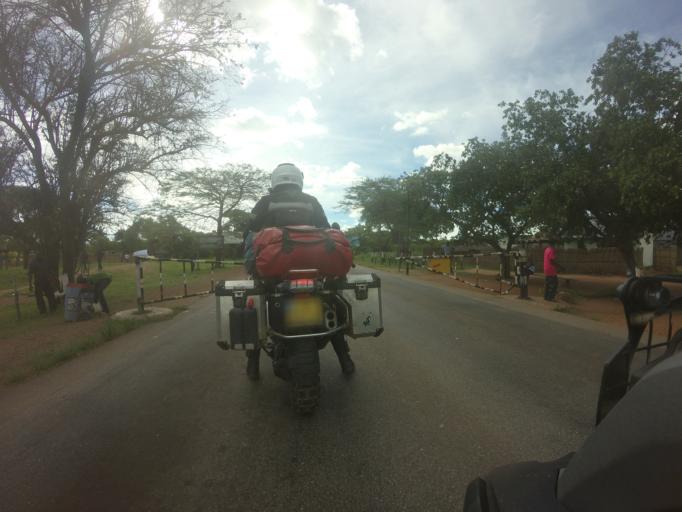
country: ZM
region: Western
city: Kaoma
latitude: -14.9049
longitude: 25.4692
